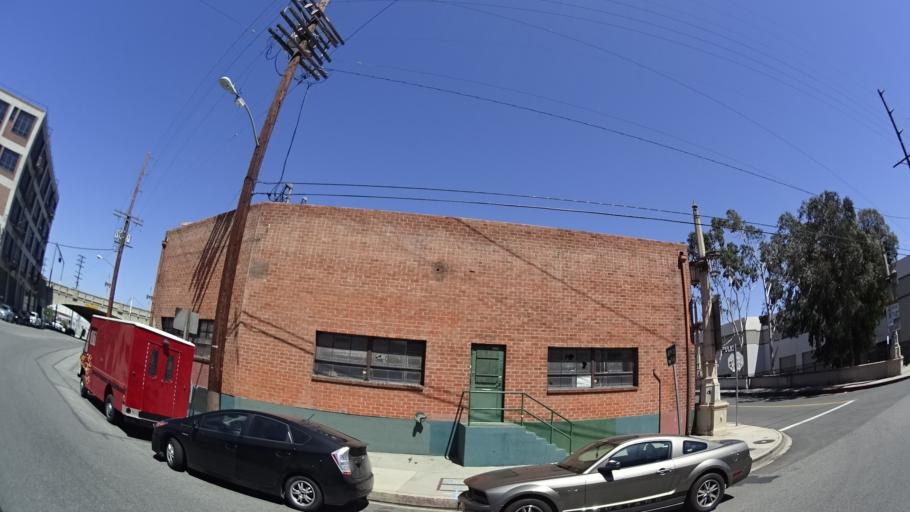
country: US
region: California
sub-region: Los Angeles County
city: Los Angeles
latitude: 34.0414
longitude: -118.2331
